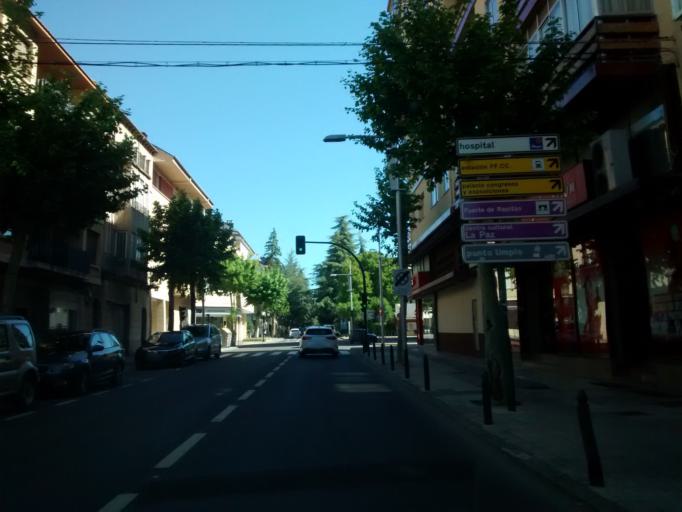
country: ES
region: Aragon
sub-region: Provincia de Huesca
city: Jaca
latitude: 42.5724
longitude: -0.5495
